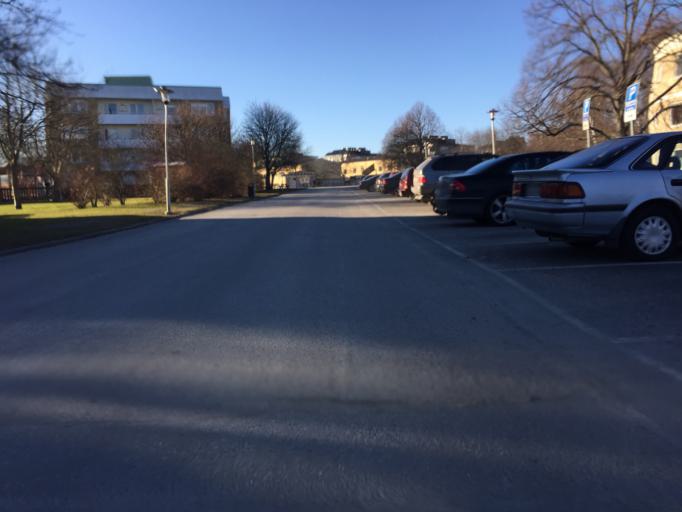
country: SE
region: Stockholm
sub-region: Stockholms Kommun
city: Bromma
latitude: 59.3560
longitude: 17.9087
